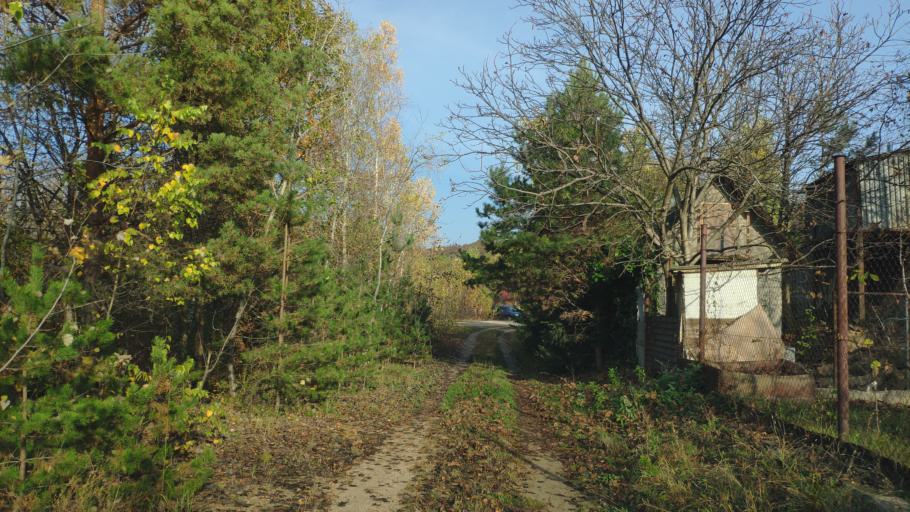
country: SK
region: Kosicky
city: Kosice
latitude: 48.7400
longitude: 21.2186
